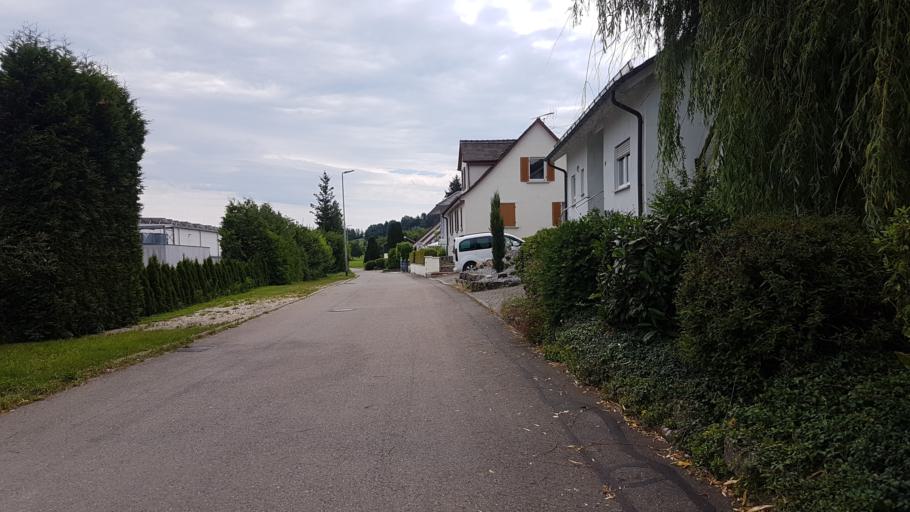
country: DE
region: Baden-Wuerttemberg
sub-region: Tuebingen Region
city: Scheer
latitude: 48.0624
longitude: 9.2982
